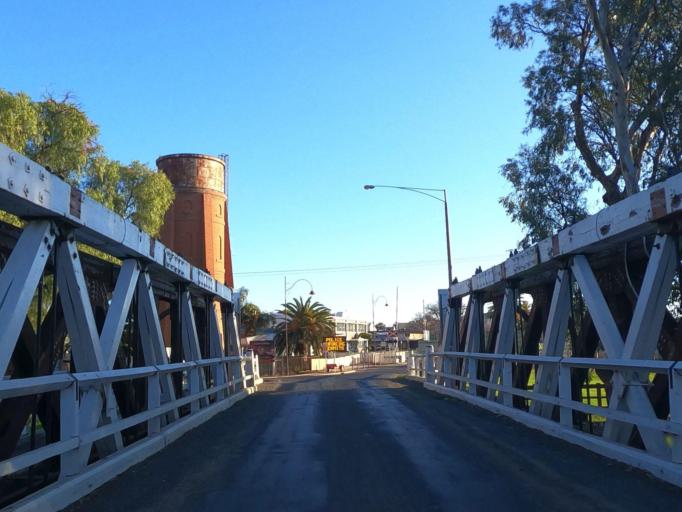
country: AU
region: Victoria
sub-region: Swan Hill
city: Swan Hill
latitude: -35.3378
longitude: 143.5626
